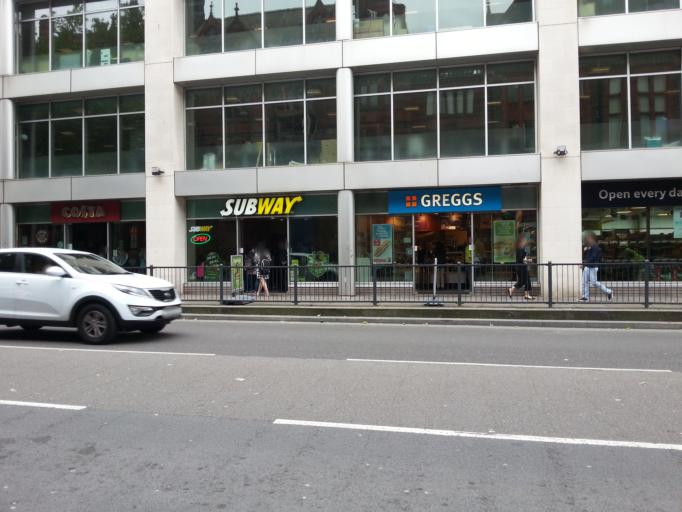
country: GB
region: England
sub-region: Liverpool
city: Liverpool
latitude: 53.4062
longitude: -2.9673
